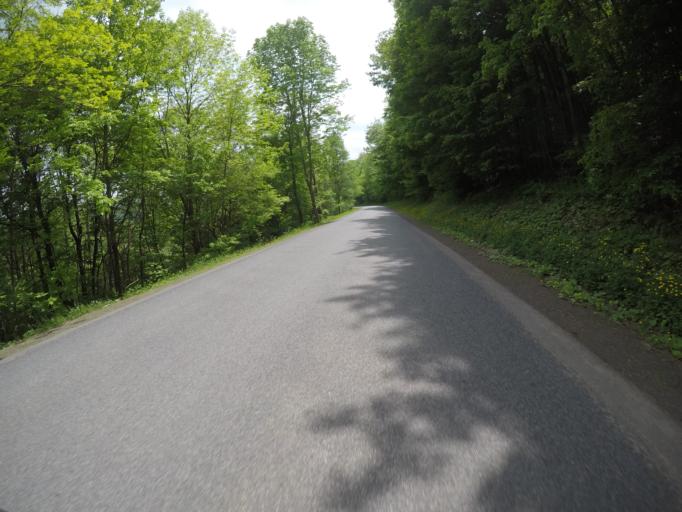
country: US
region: New York
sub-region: Delaware County
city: Stamford
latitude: 42.2300
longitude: -74.6928
